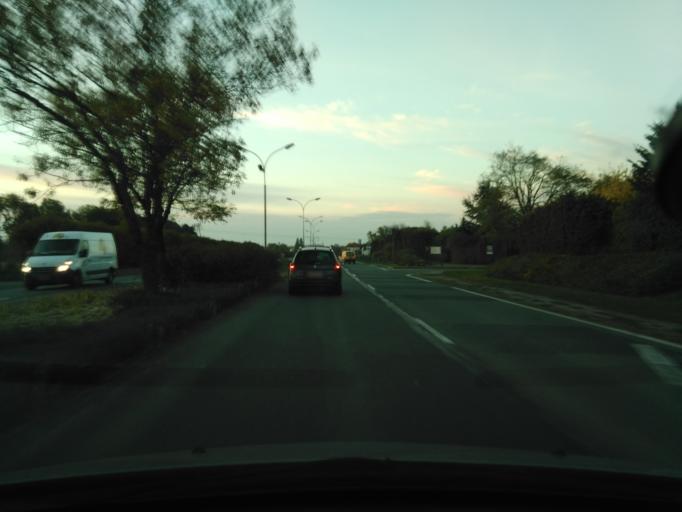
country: FR
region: Poitou-Charentes
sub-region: Departement de la Charente-Maritime
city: Lagord
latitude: 46.1836
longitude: -1.1524
